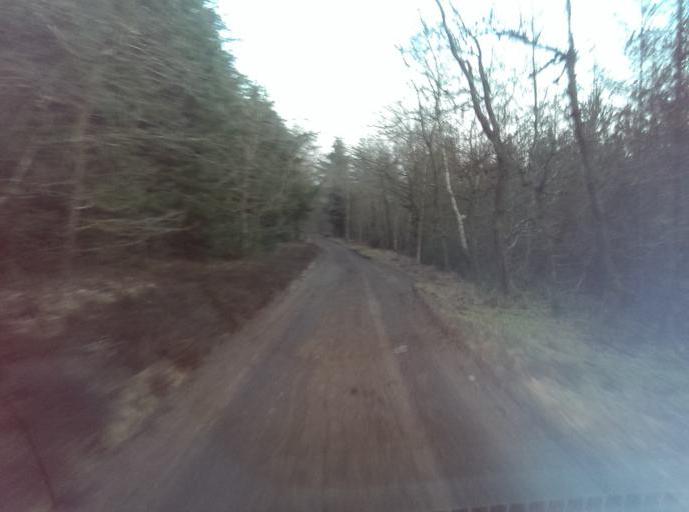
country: DK
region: South Denmark
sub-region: Varde Kommune
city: Oksbol
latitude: 55.5608
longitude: 8.3032
